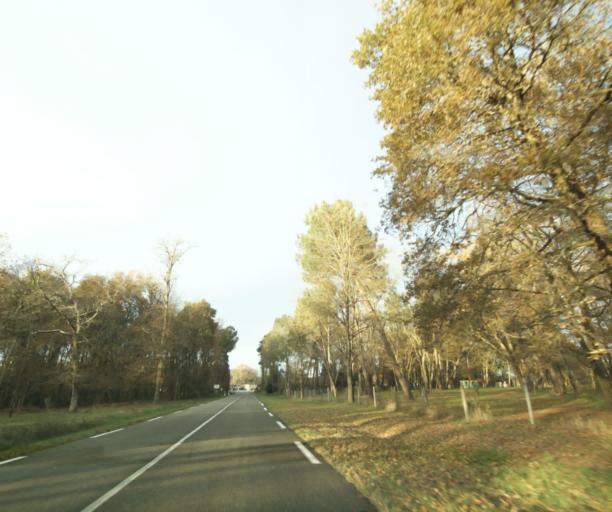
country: FR
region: Aquitaine
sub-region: Departement des Landes
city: Gabarret
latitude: 44.1009
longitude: -0.1044
